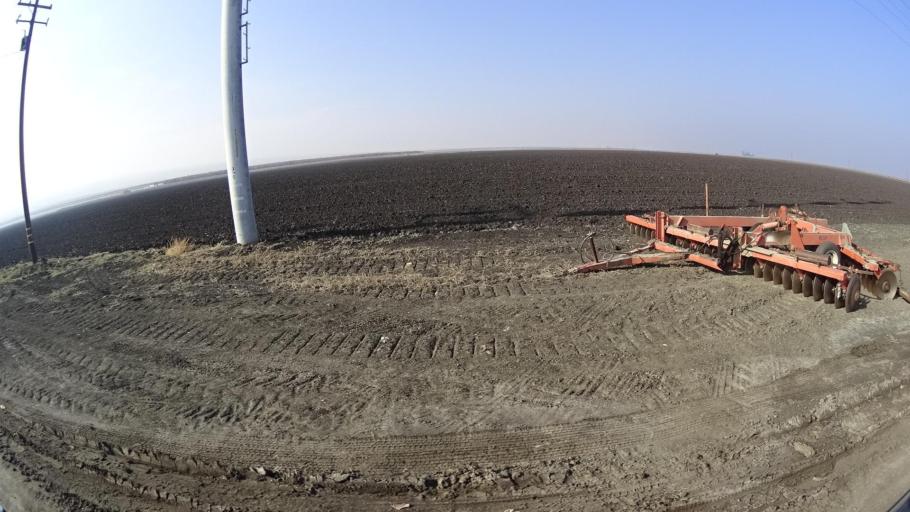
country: US
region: California
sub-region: Kern County
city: Buttonwillow
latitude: 35.3511
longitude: -119.4476
